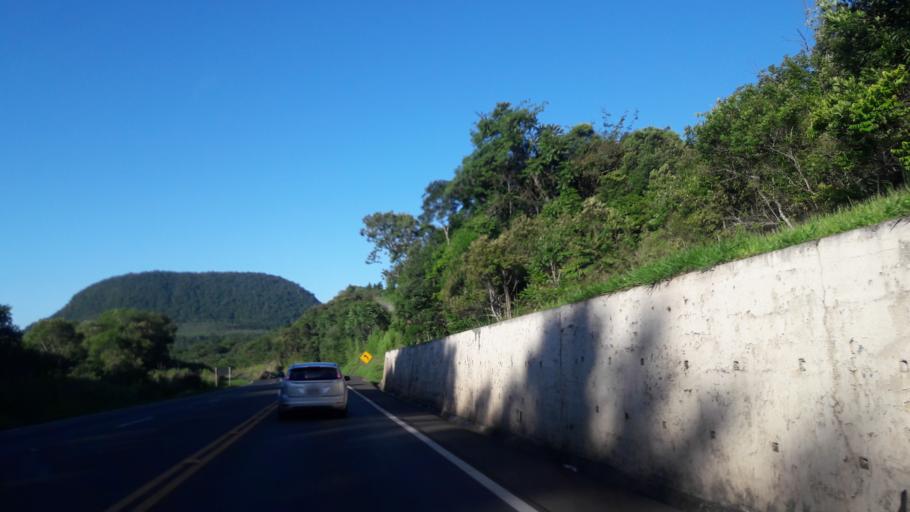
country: BR
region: Parana
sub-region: Prudentopolis
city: Prudentopolis
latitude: -25.3212
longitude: -51.1902
